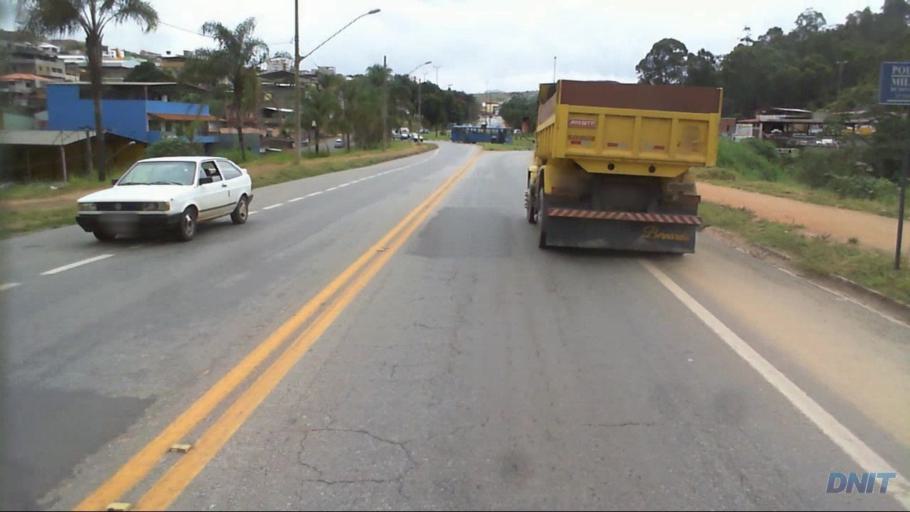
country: BR
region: Minas Gerais
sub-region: Joao Monlevade
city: Joao Monlevade
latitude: -19.8396
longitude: -43.1801
